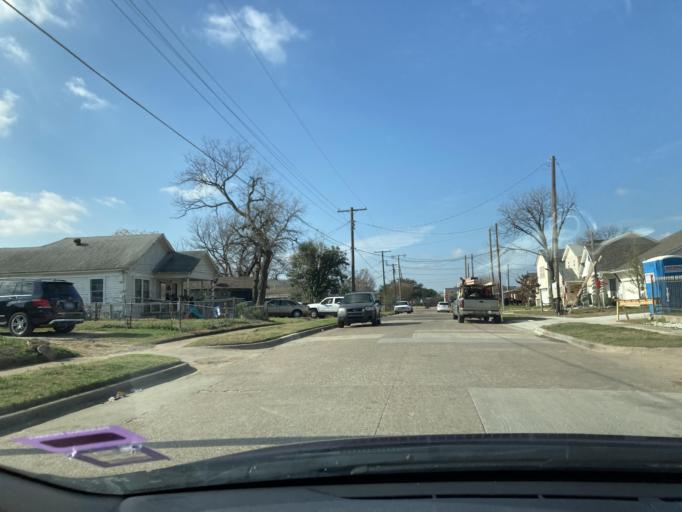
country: US
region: Texas
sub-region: Dallas County
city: Dallas
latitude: 32.7904
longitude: -96.8548
